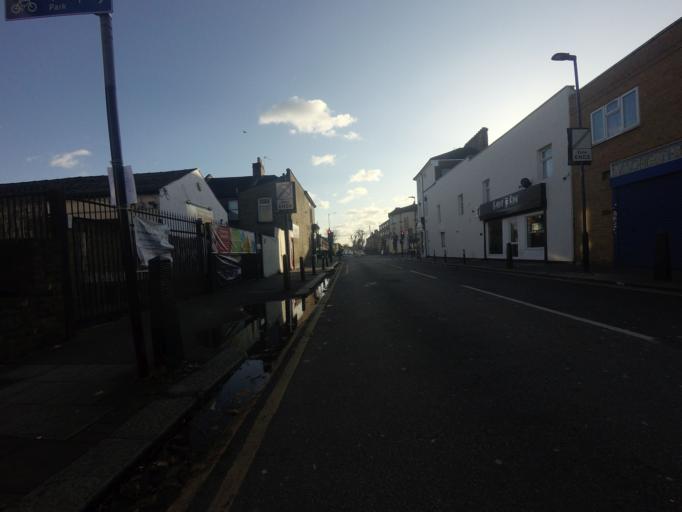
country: GB
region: England
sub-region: Greater London
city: East Ham
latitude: 51.5480
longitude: 0.0358
